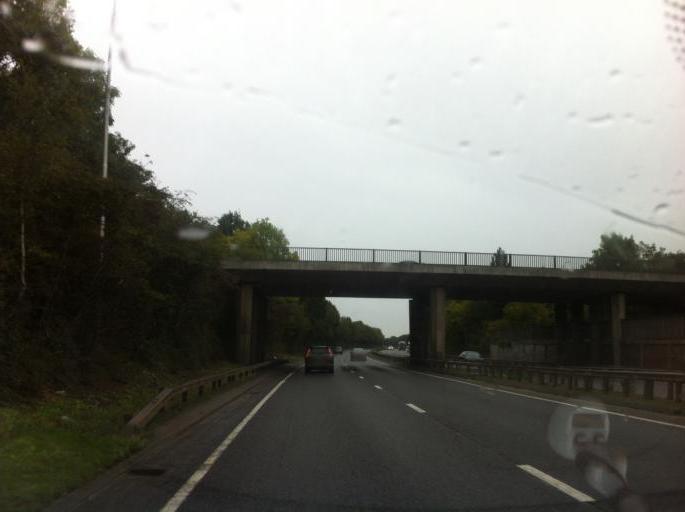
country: GB
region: England
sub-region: Peterborough
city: Eye
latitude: 52.5882
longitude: -0.2151
